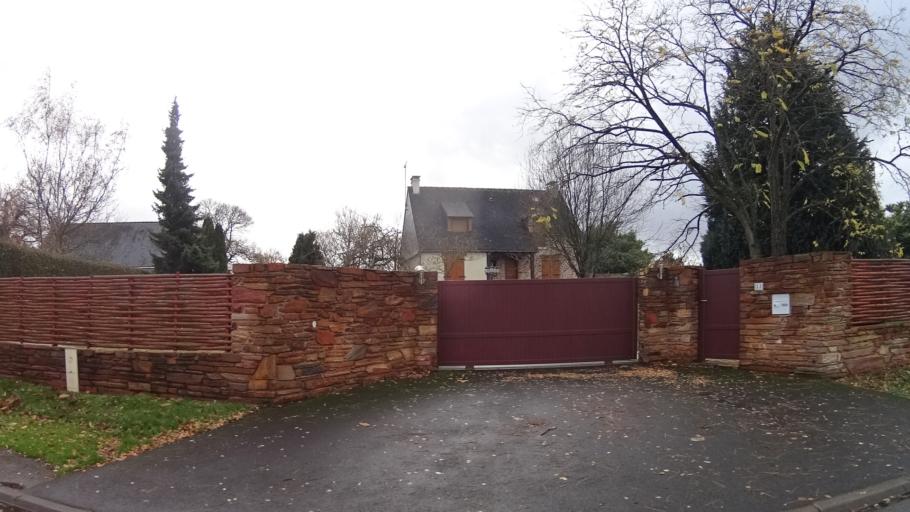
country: FR
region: Brittany
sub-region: Departement du Morbihan
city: Rieux
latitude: 47.5702
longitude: -2.1178
